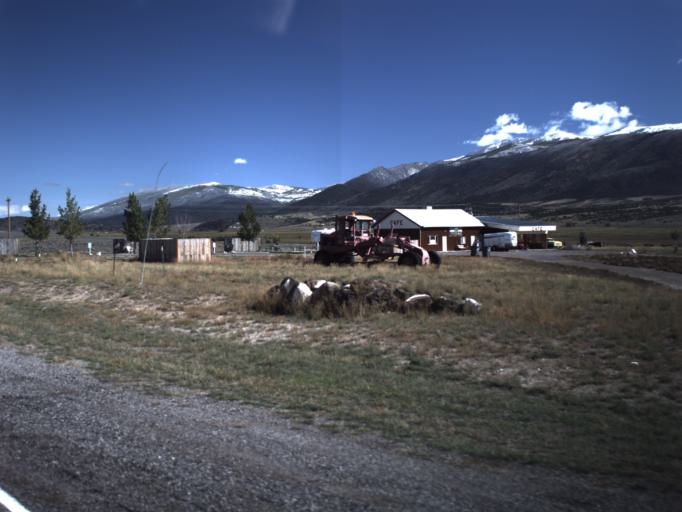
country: US
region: Utah
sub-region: Sevier County
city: Monroe
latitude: 38.5207
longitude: -111.8813
